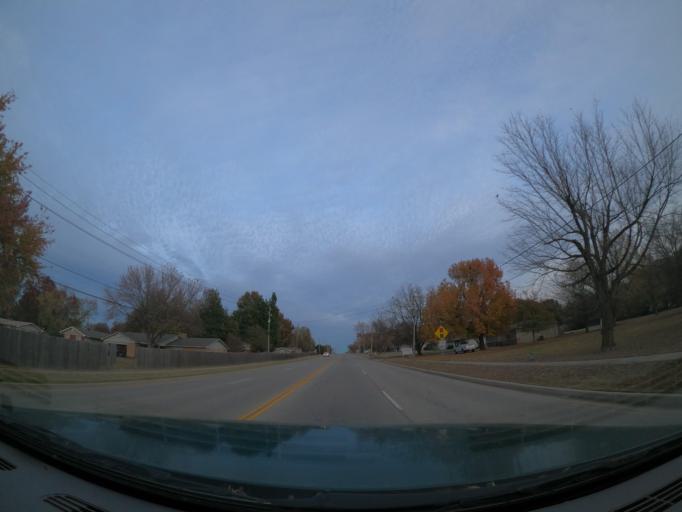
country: US
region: Oklahoma
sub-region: Tulsa County
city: Broken Arrow
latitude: 36.0319
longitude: -95.7949
